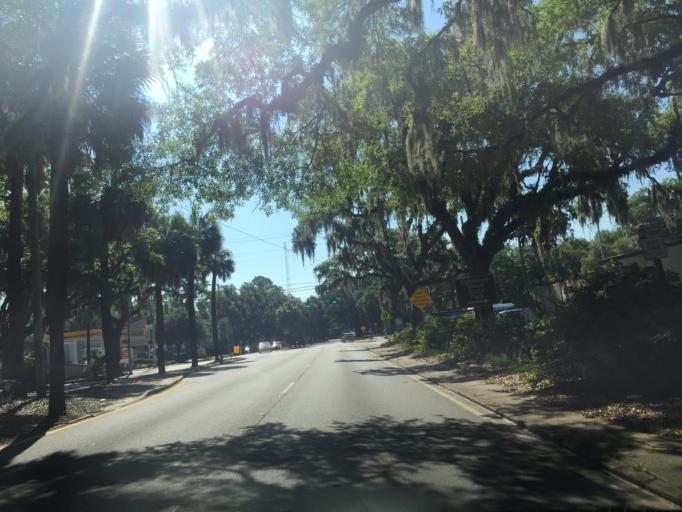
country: US
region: Georgia
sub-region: Chatham County
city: Savannah
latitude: 32.0485
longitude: -81.0861
